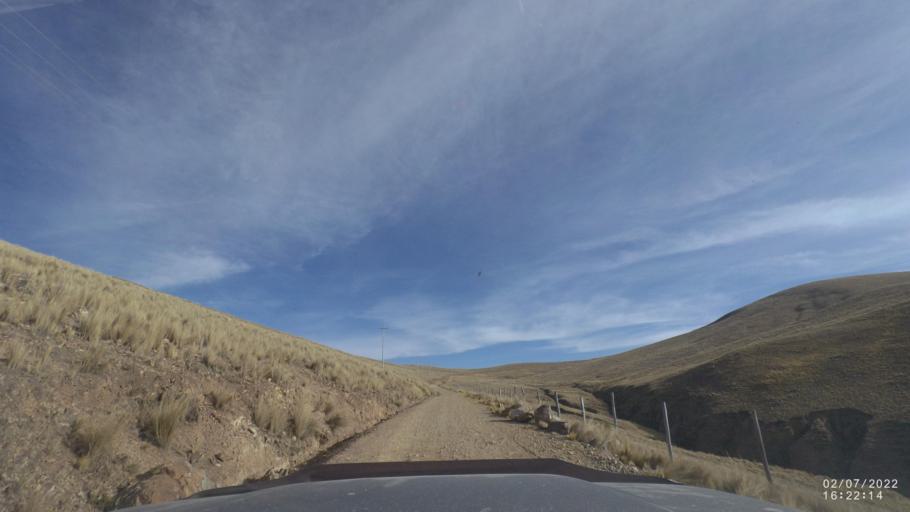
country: BO
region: Cochabamba
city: Irpa Irpa
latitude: -17.9339
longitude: -66.4553
